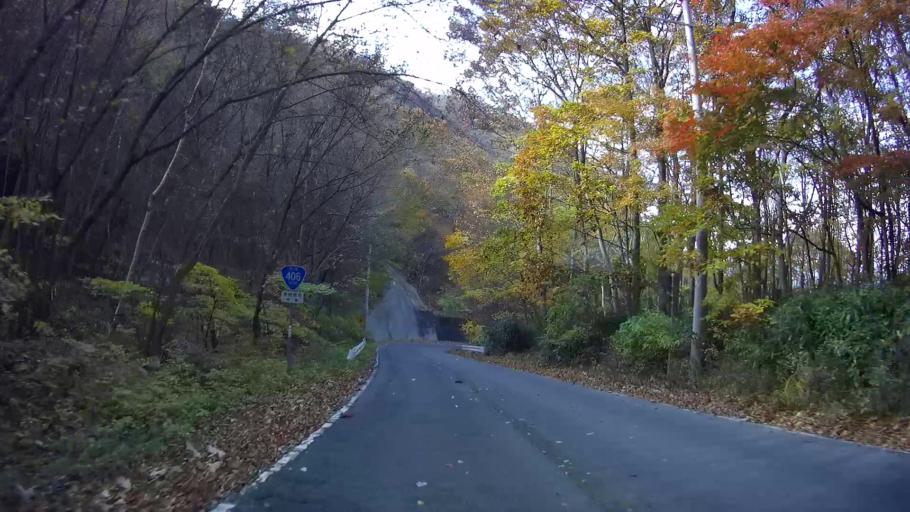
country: JP
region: Gunma
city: Nakanojomachi
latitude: 36.5268
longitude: 138.6598
